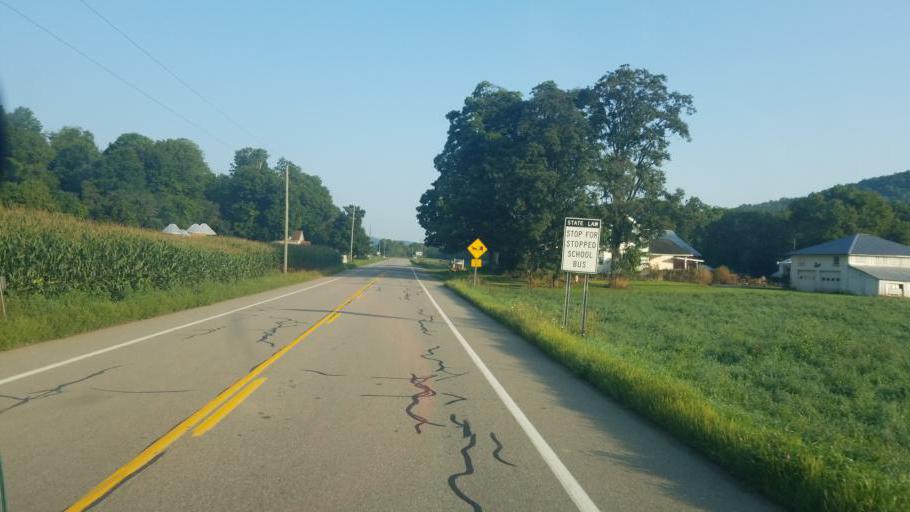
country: US
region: Pennsylvania
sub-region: Tioga County
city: Westfield
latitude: 42.0010
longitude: -77.5050
